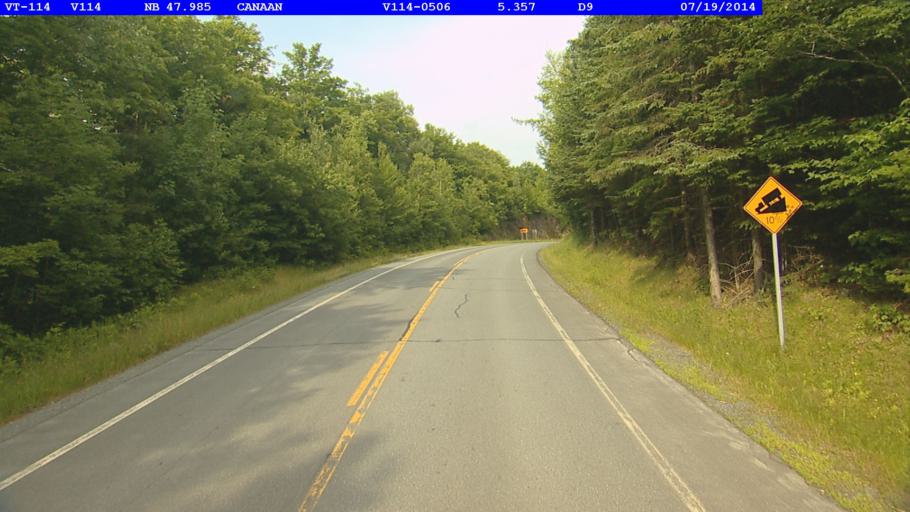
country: US
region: New Hampshire
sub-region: Coos County
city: Colebrook
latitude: 45.0089
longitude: -71.5884
